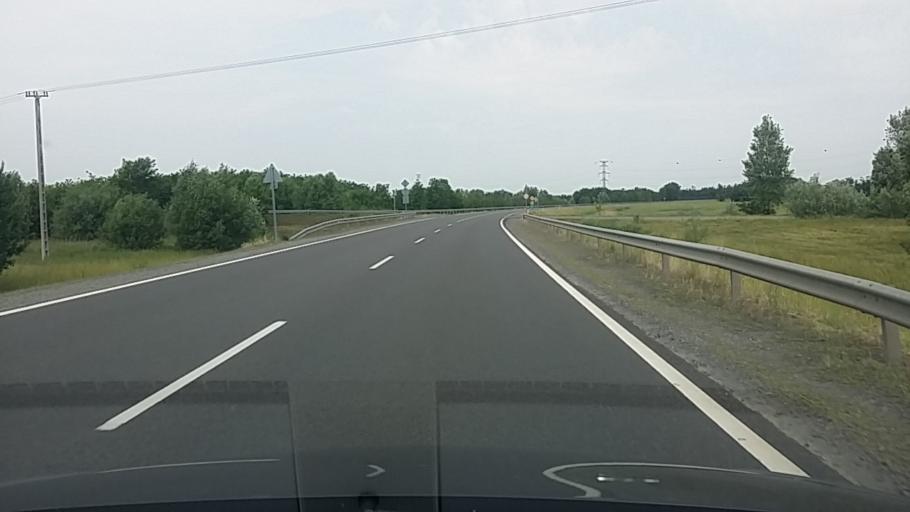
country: HU
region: Szabolcs-Szatmar-Bereg
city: Nyirpazony
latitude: 47.9592
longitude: 21.8168
